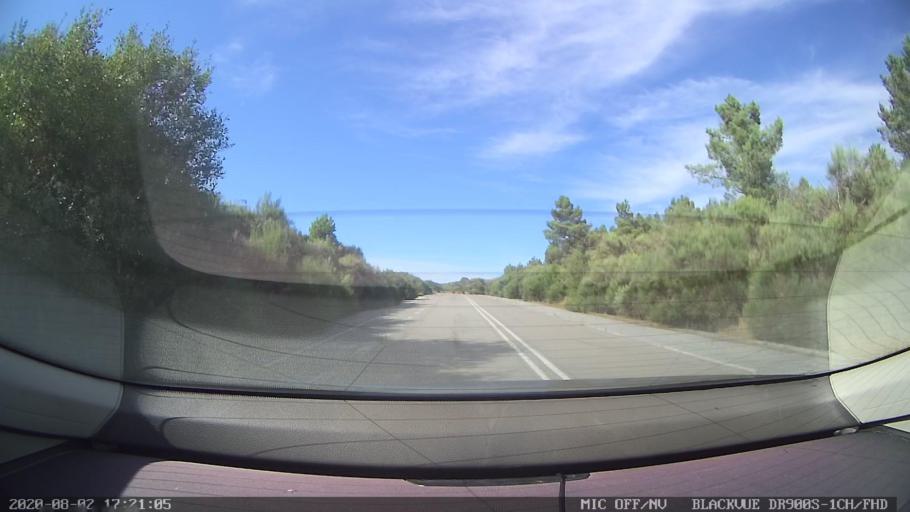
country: PT
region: Vila Real
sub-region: Murca
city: Murca
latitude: 41.3709
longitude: -7.5515
